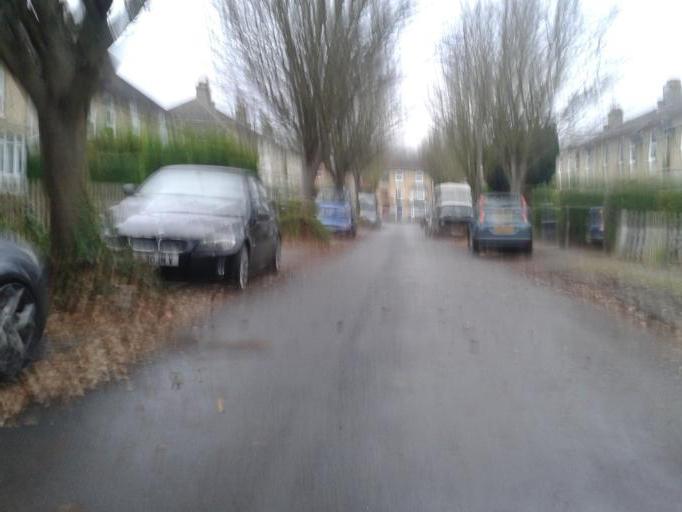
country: GB
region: England
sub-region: Cambridgeshire
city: Cambridge
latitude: 52.2043
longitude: 0.1532
